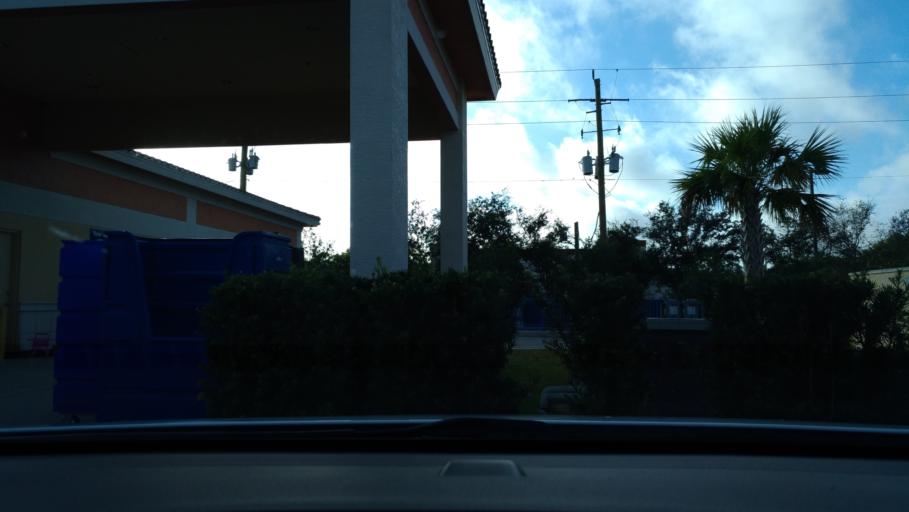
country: US
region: Florida
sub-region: Lee County
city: Estero
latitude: 26.4322
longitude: -81.7835
